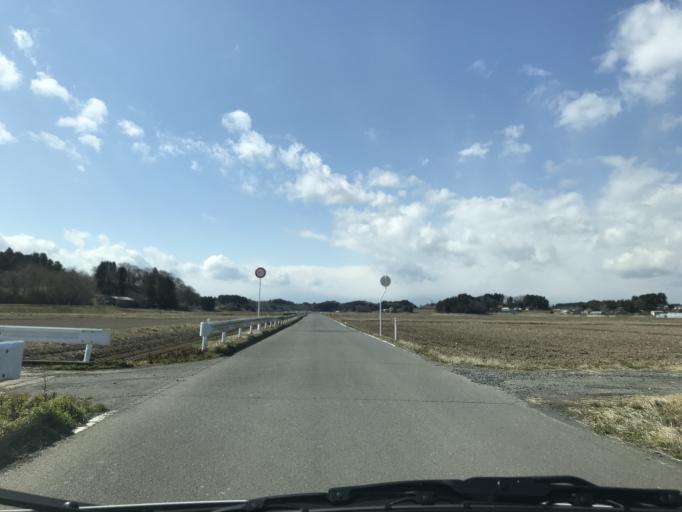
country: JP
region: Miyagi
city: Wakuya
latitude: 38.6758
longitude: 141.1369
